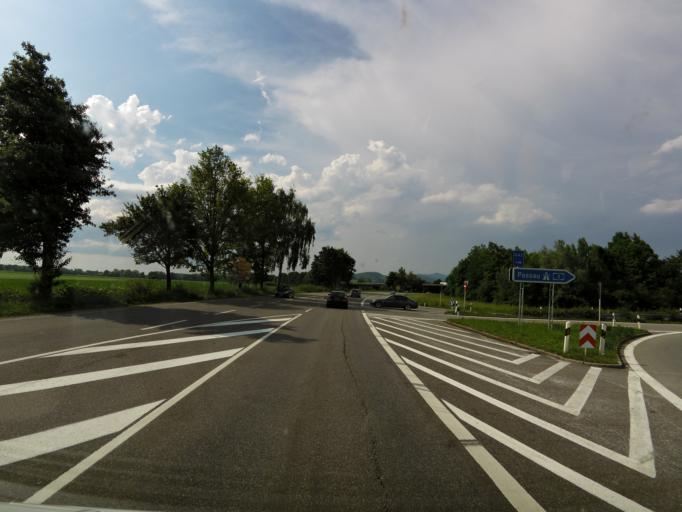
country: DE
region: Bavaria
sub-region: Lower Bavaria
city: Hengersberg
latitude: 48.7681
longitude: 13.0415
